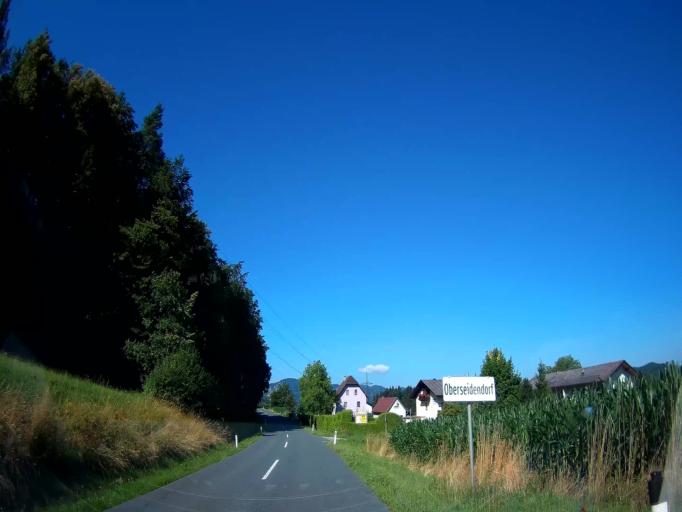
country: AT
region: Carinthia
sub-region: Politischer Bezirk Volkermarkt
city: Gallizien
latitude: 46.6163
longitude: 14.5567
